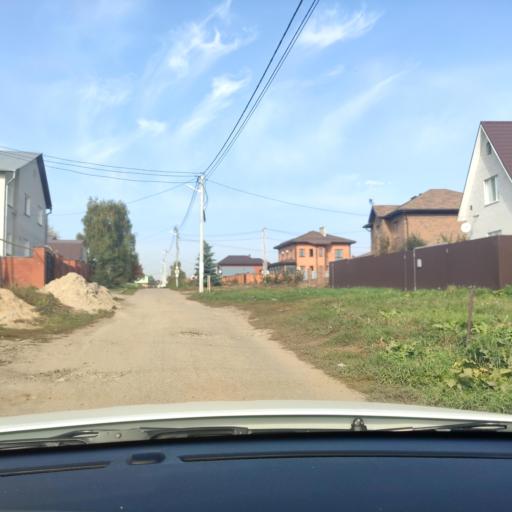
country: RU
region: Tatarstan
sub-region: Gorod Kazan'
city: Kazan
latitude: 55.8101
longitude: 49.2074
